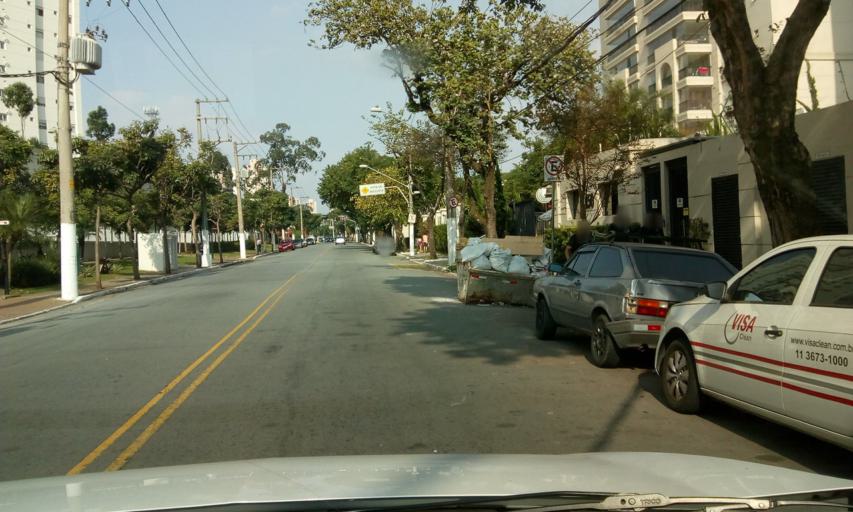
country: BR
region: Sao Paulo
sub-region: Sao Paulo
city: Sao Paulo
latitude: -23.5510
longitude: -46.5947
